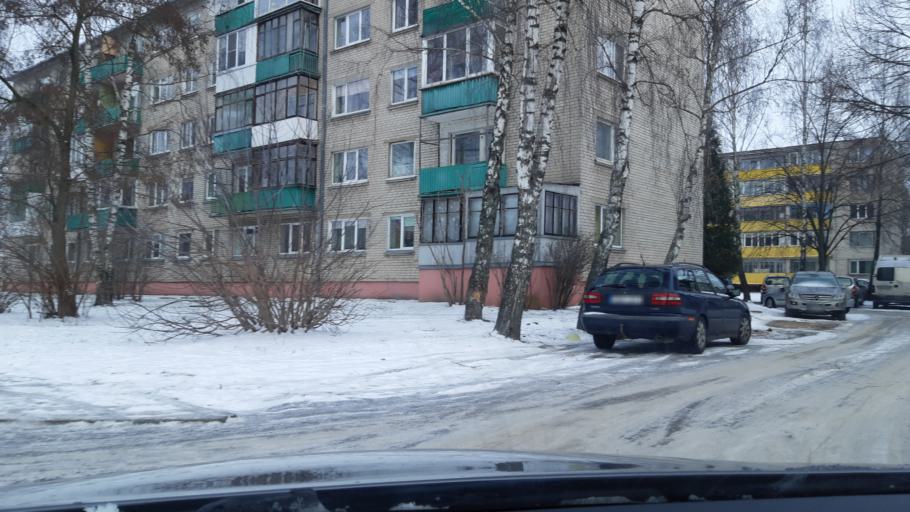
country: LT
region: Kauno apskritis
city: Kedainiai
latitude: 55.2913
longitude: 23.9844
